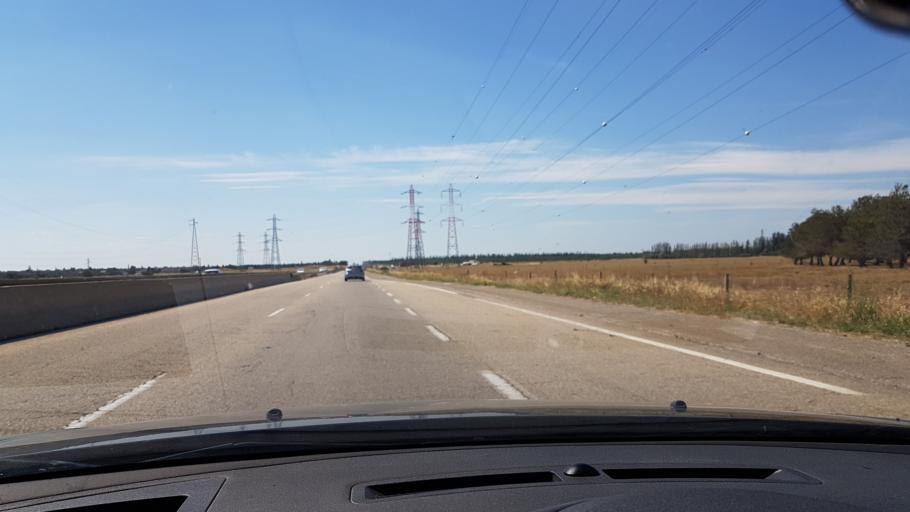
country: FR
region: Provence-Alpes-Cote d'Azur
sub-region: Departement des Bouches-du-Rhone
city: Fos-sur-Mer
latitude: 43.4825
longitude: 4.8919
